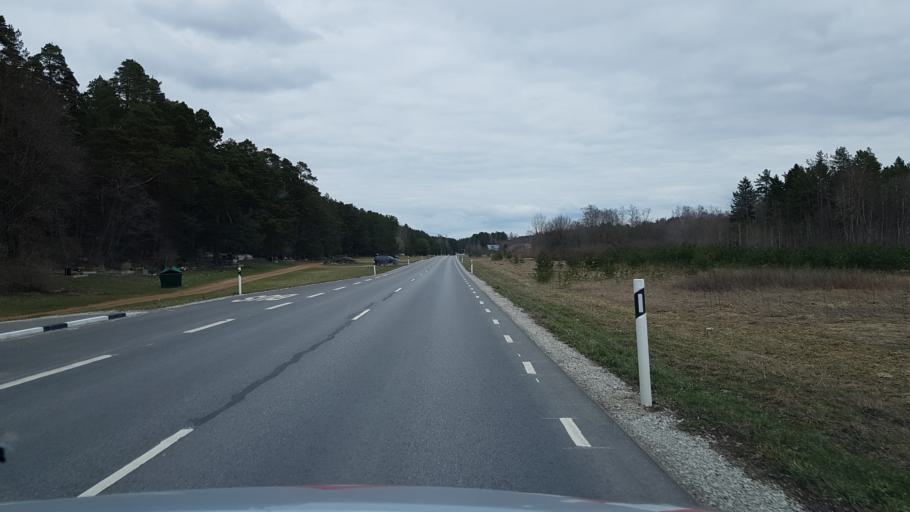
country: EE
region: Ida-Virumaa
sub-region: Narva-Joesuu linn
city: Narva-Joesuu
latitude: 59.4149
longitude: 28.0905
